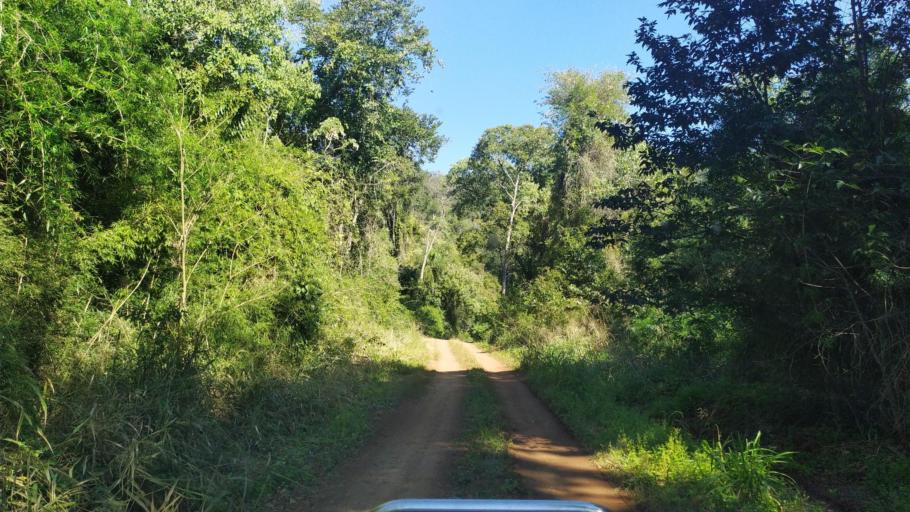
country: AR
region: Misiones
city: El Alcazar
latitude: -26.7593
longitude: -54.5820
